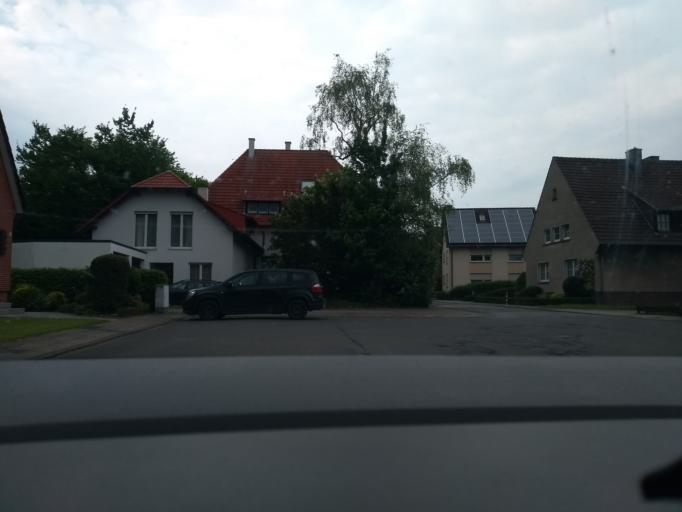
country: DE
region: North Rhine-Westphalia
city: Selm
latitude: 51.6640
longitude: 7.4638
